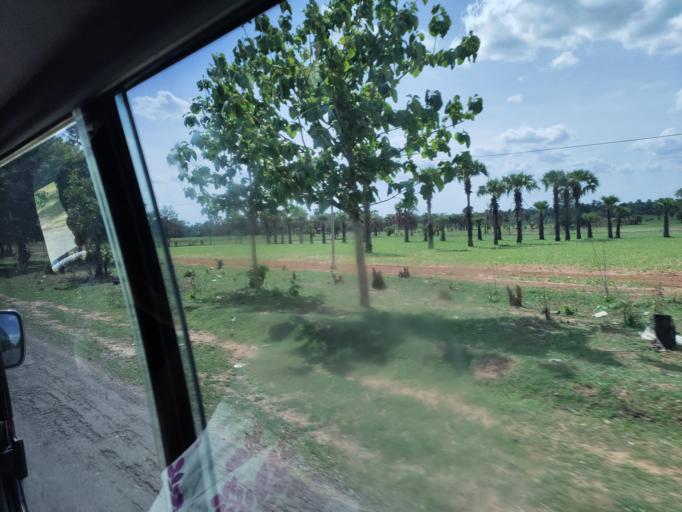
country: MM
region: Magway
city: Chauk
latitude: 20.8201
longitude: 95.0660
